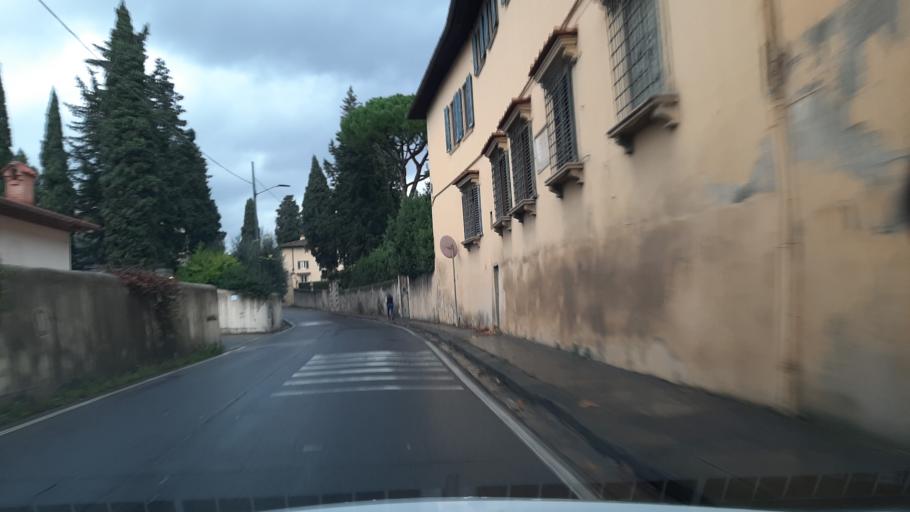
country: IT
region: Tuscany
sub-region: Province of Florence
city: Florence
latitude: 43.7962
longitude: 11.2620
